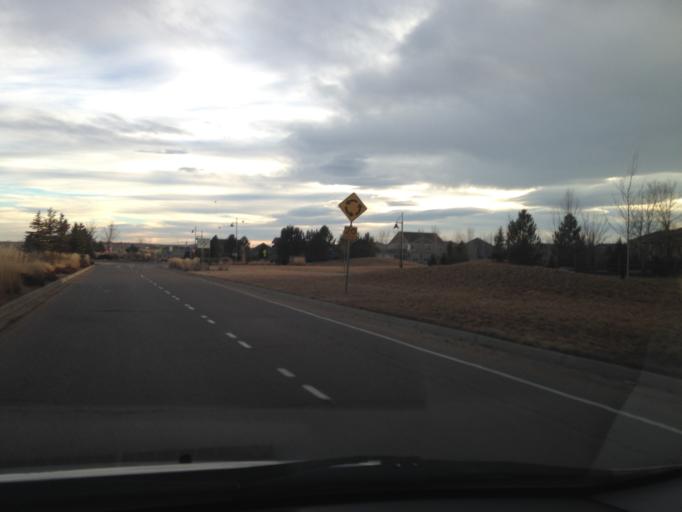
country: US
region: Colorado
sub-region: Weld County
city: Dacono
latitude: 40.0938
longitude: -104.9990
